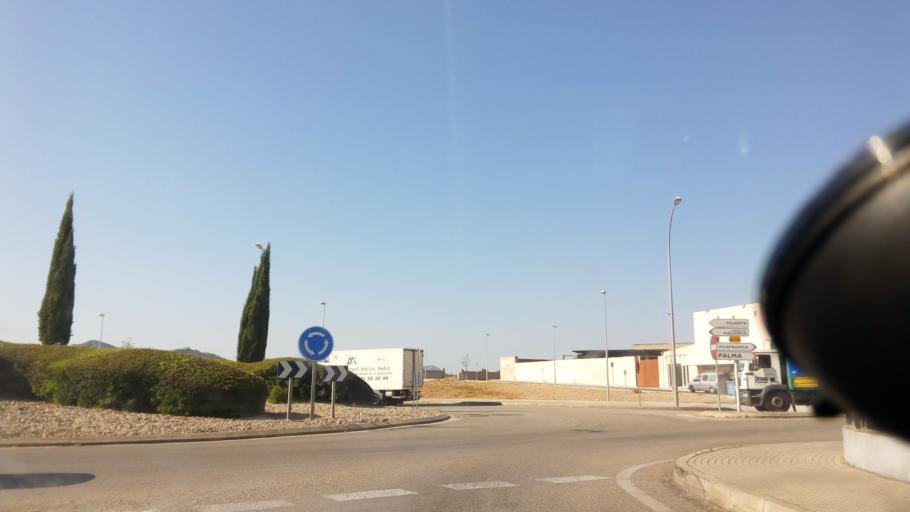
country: ES
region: Balearic Islands
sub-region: Illes Balears
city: Manacor
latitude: 39.5726
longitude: 3.1946
